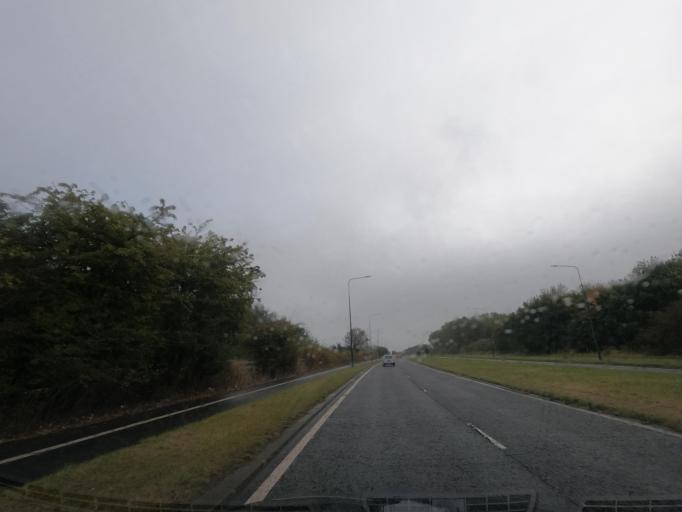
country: GB
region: England
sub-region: Redcar and Cleveland
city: Redcar
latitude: 54.6091
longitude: -1.1045
